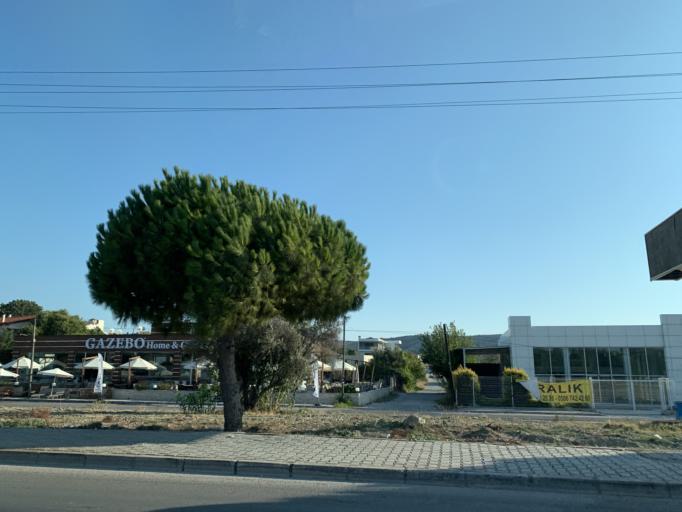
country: TR
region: Izmir
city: Alacati
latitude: 38.3094
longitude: 26.3509
